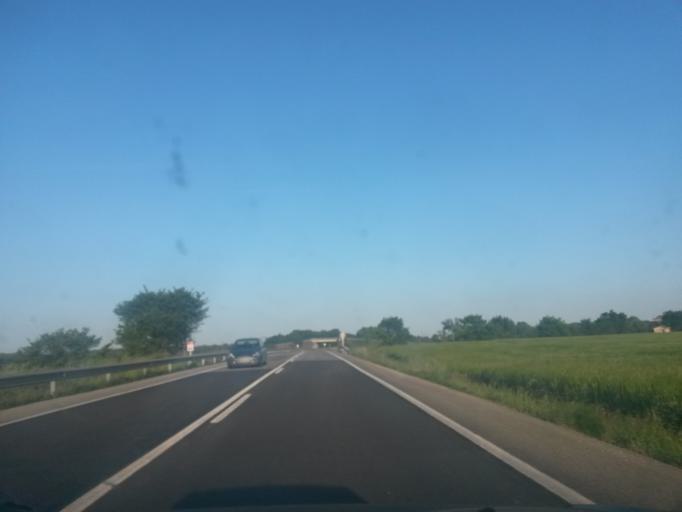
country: ES
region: Catalonia
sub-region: Provincia de Girona
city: Banyoles
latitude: 42.1536
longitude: 2.7544
